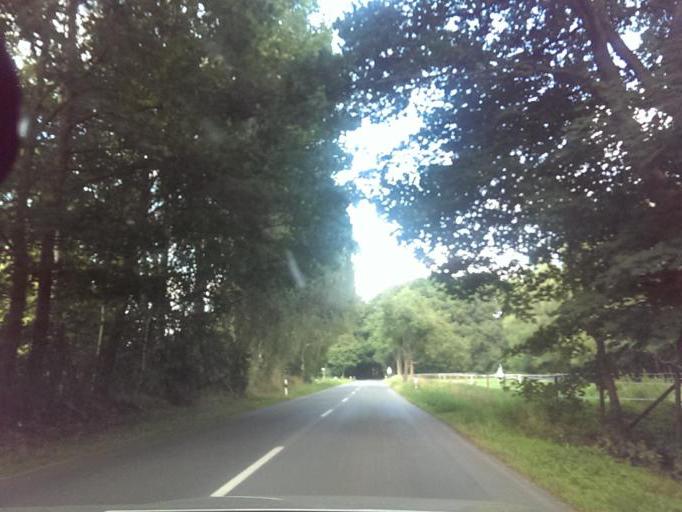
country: DE
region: North Rhine-Westphalia
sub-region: Regierungsbezirk Detmold
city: Delbruck
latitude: 51.7515
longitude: 8.6113
